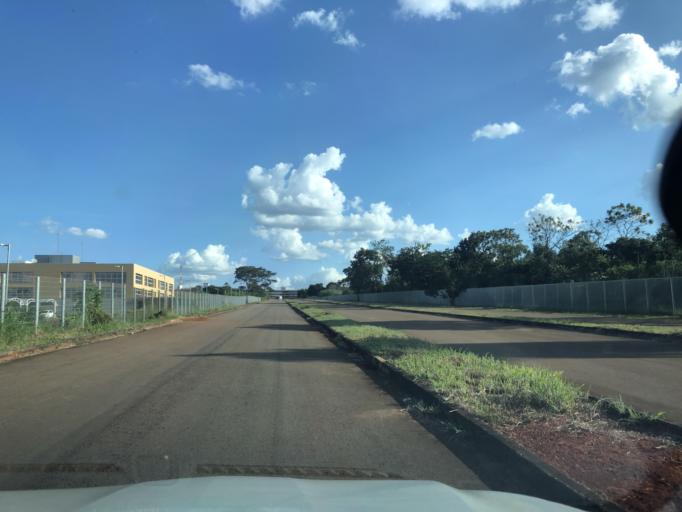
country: BR
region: Federal District
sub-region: Brasilia
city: Brasilia
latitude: -15.7377
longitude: -47.9056
